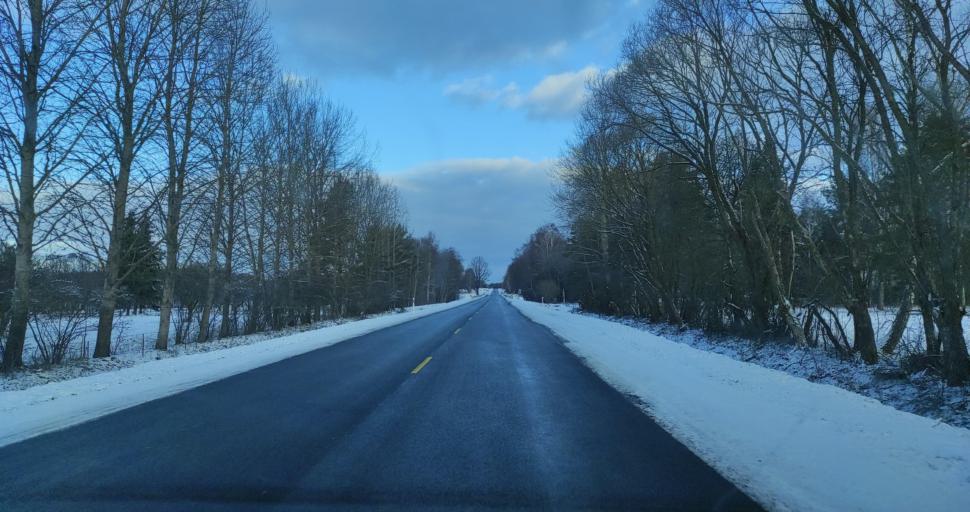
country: LV
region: Skrunda
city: Skrunda
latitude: 56.7110
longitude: 22.0129
